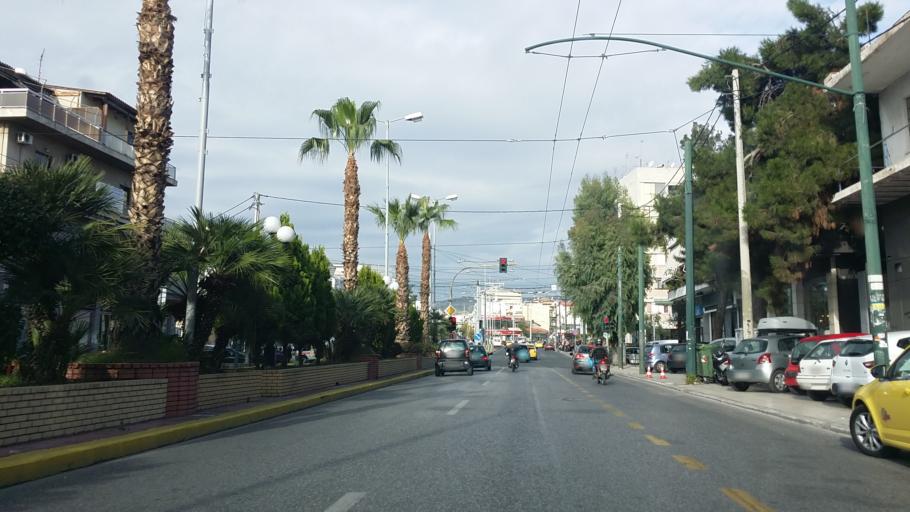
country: GR
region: Attica
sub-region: Nomarchia Athinas
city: Peristeri
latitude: 38.0053
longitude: 23.7009
